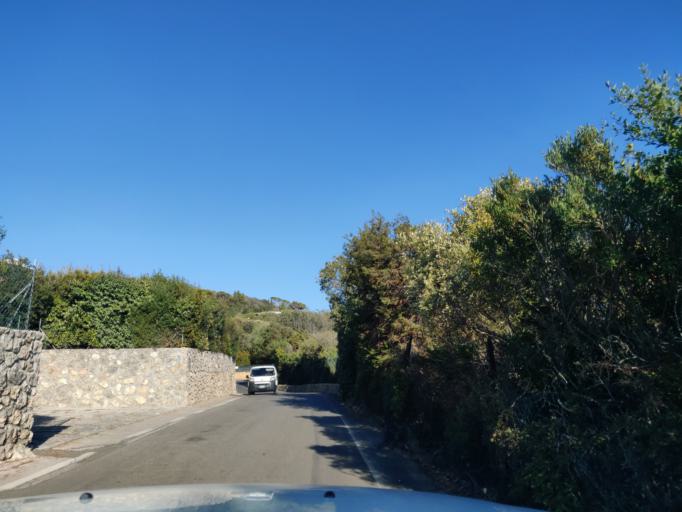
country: IT
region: Tuscany
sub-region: Provincia di Grosseto
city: Orbetello Scalo
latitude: 42.4088
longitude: 11.2820
